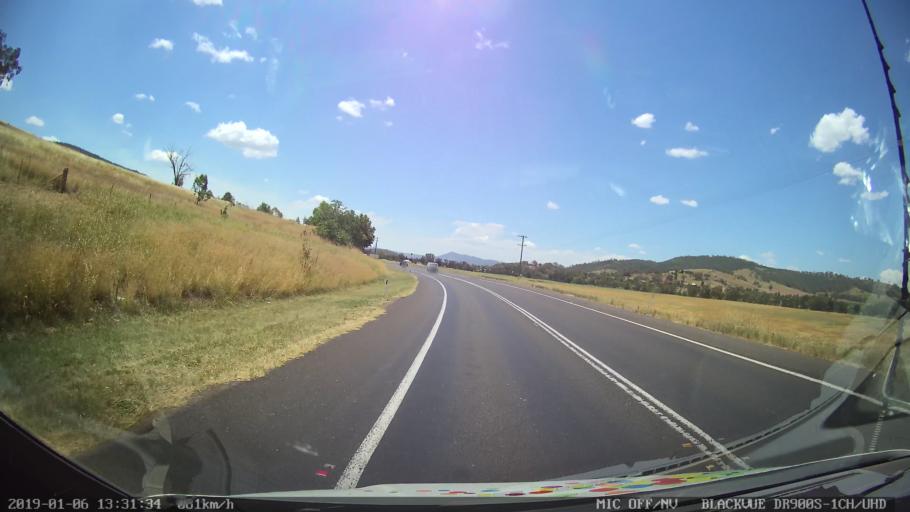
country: AU
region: New South Wales
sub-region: Tamworth Municipality
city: East Tamworth
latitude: -31.1204
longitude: 150.9945
